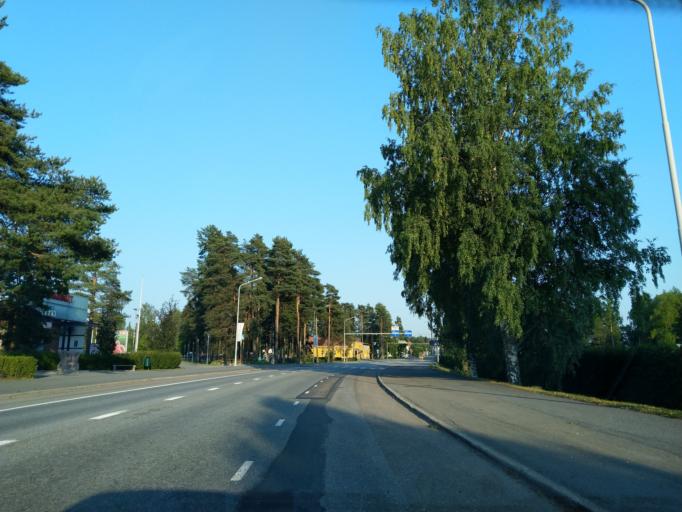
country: FI
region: Satakunta
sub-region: Pohjois-Satakunta
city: Kankaanpaeae
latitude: 61.8070
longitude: 22.3884
